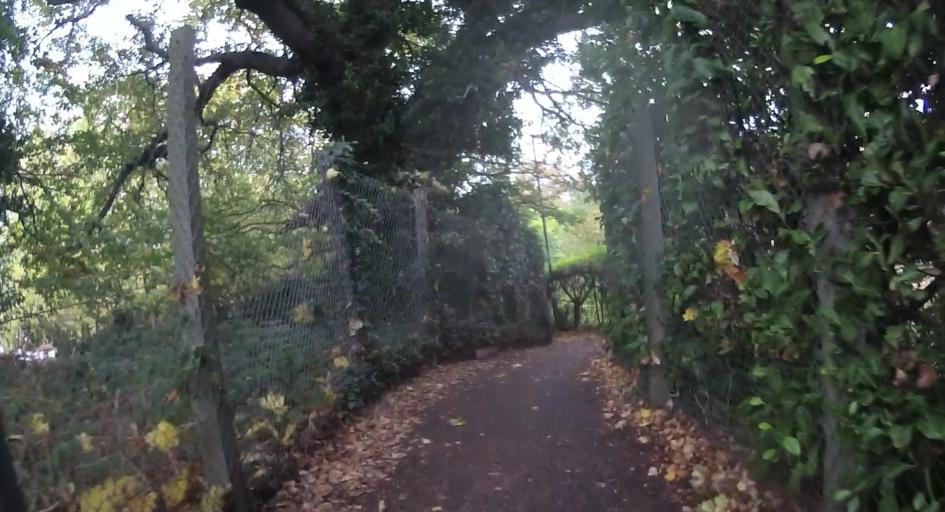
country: GB
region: England
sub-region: Surrey
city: West Byfleet
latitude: 51.3410
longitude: -0.4988
